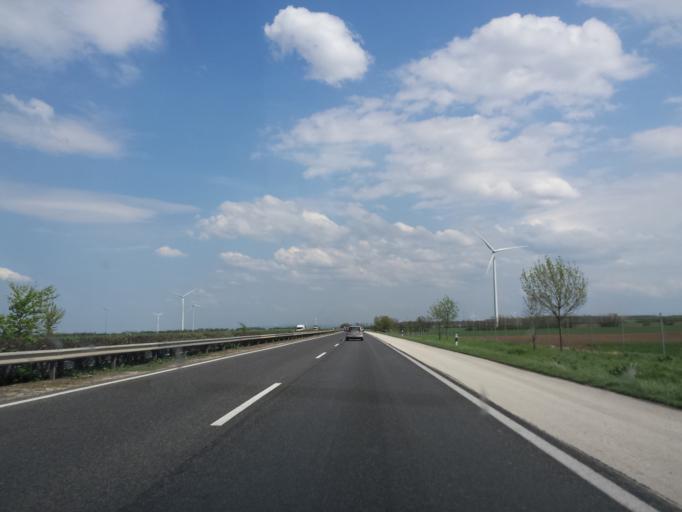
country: HU
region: Gyor-Moson-Sopron
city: Bony
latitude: 47.6796
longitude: 17.9221
